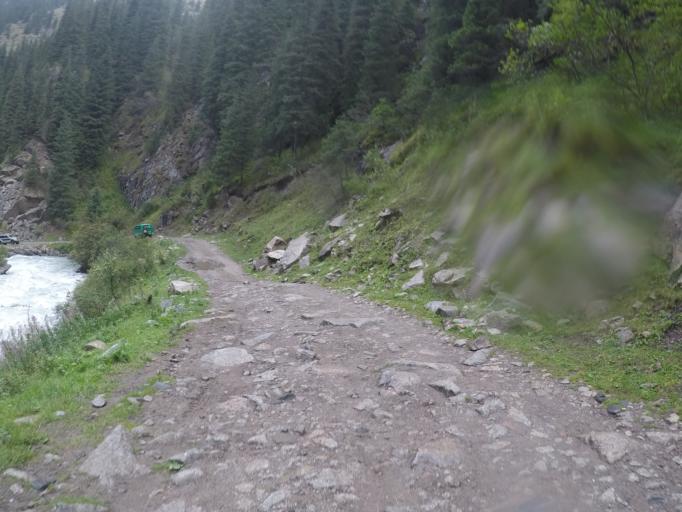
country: KG
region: Ysyk-Koel
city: Teploklyuchenka
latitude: 42.4159
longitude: 78.5717
